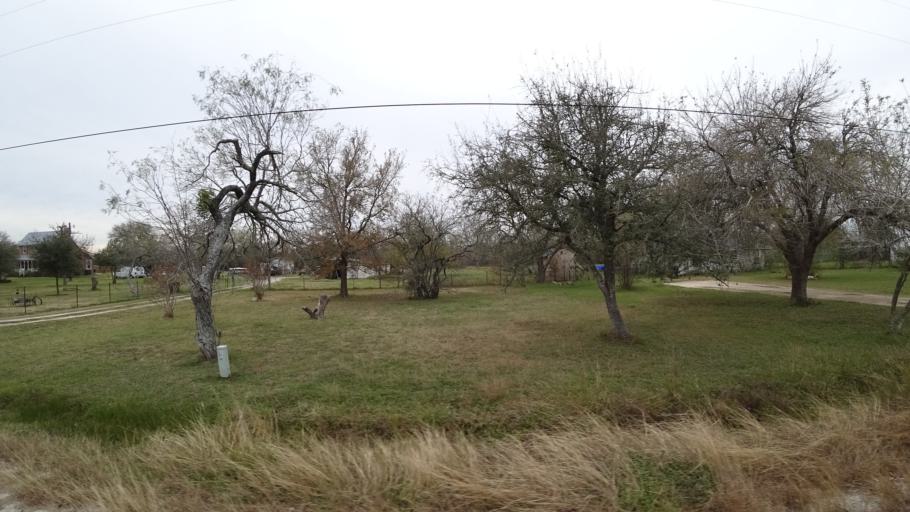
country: US
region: Texas
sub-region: Travis County
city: Garfield
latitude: 30.1059
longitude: -97.5758
